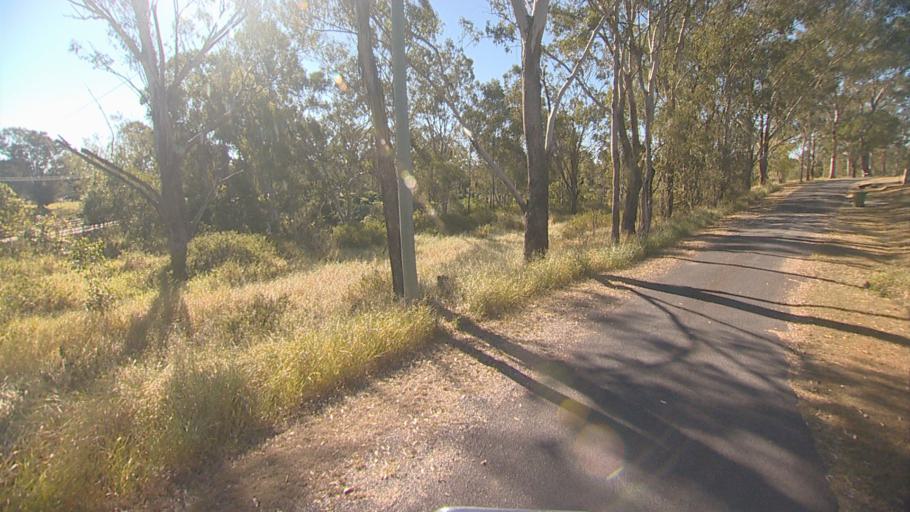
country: AU
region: Queensland
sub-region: Logan
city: North Maclean
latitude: -27.7859
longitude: 153.0129
